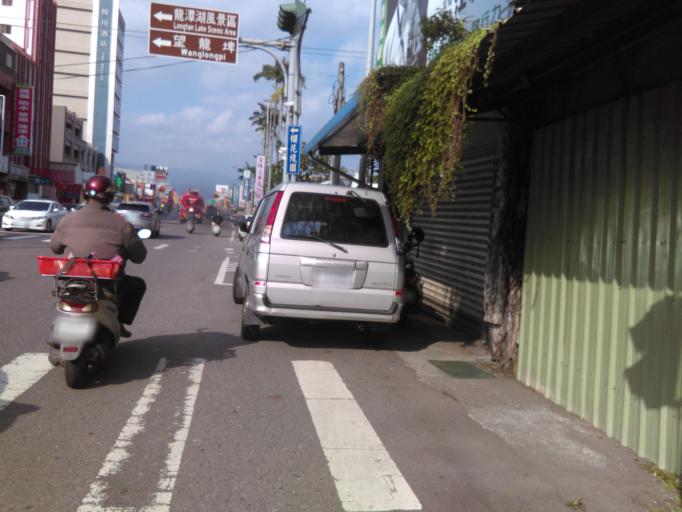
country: TW
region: Taiwan
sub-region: Yilan
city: Yilan
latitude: 24.7686
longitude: 121.7564
